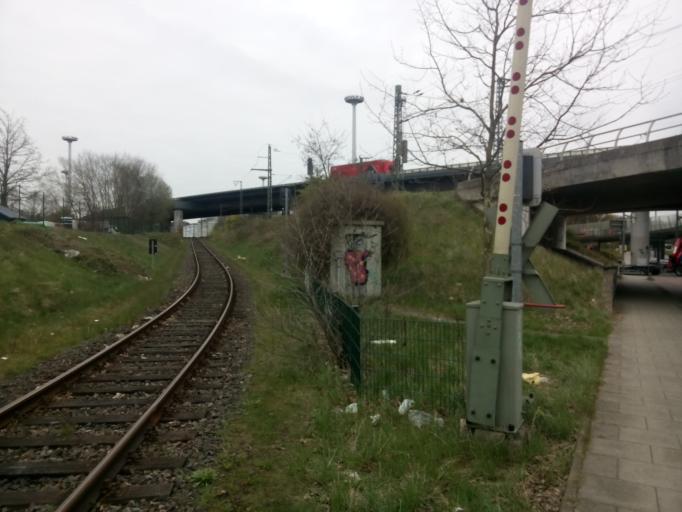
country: DE
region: Bremen
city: Bremen
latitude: 53.0829
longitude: 8.7913
